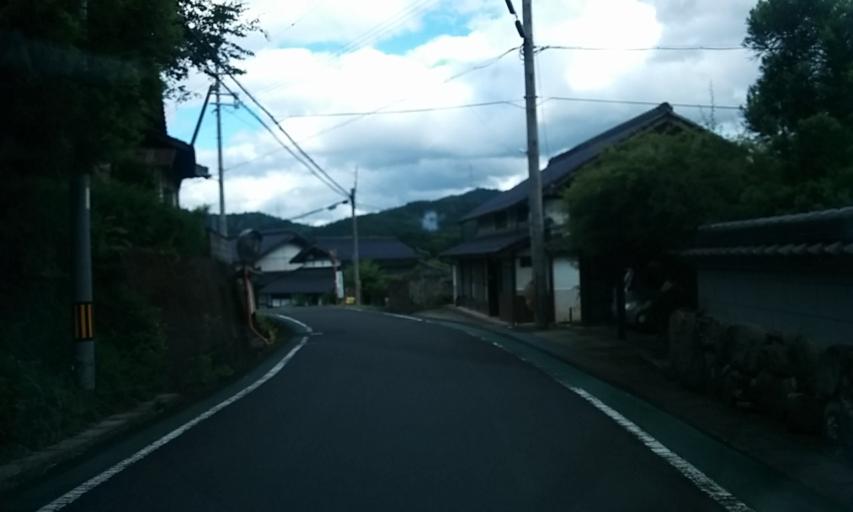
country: JP
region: Kyoto
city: Ayabe
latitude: 35.3654
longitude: 135.2463
